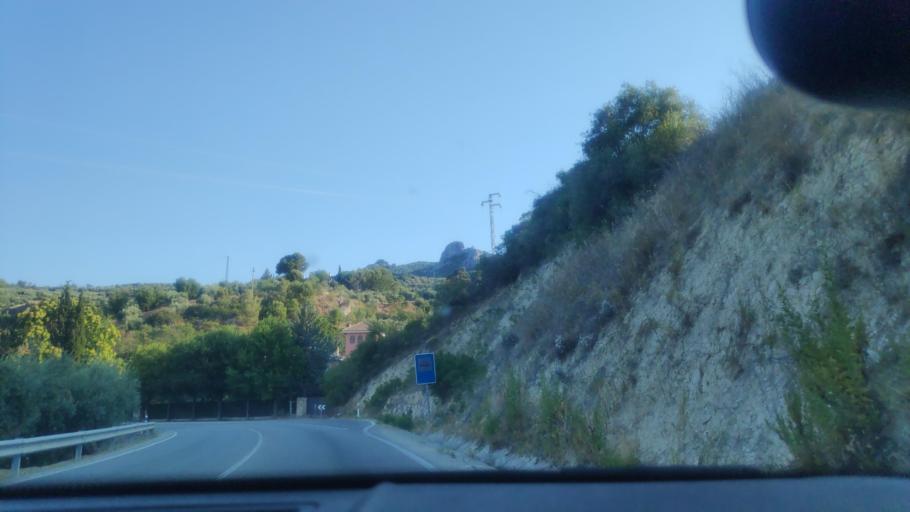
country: ES
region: Andalusia
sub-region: Provincia de Jaen
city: Jaen
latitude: 37.7472
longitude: -3.7906
